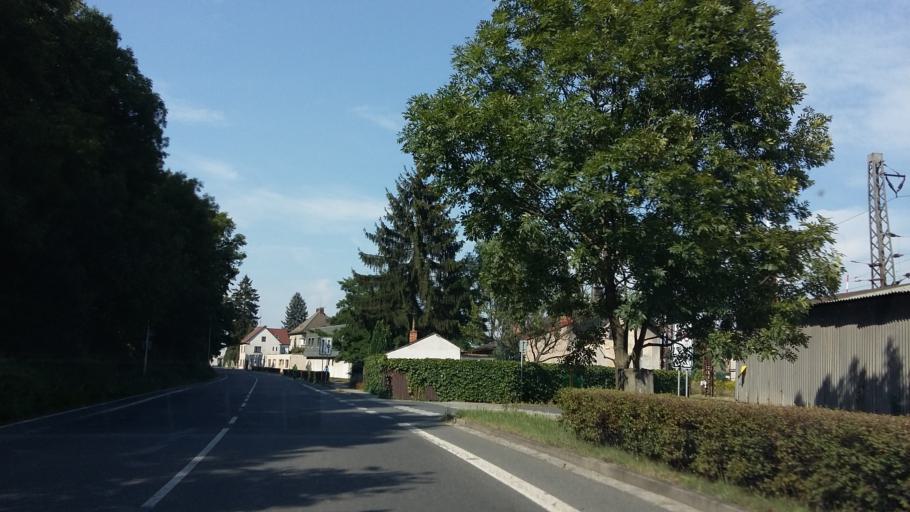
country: CZ
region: Central Bohemia
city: Velky Osek
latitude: 50.1054
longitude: 15.1922
